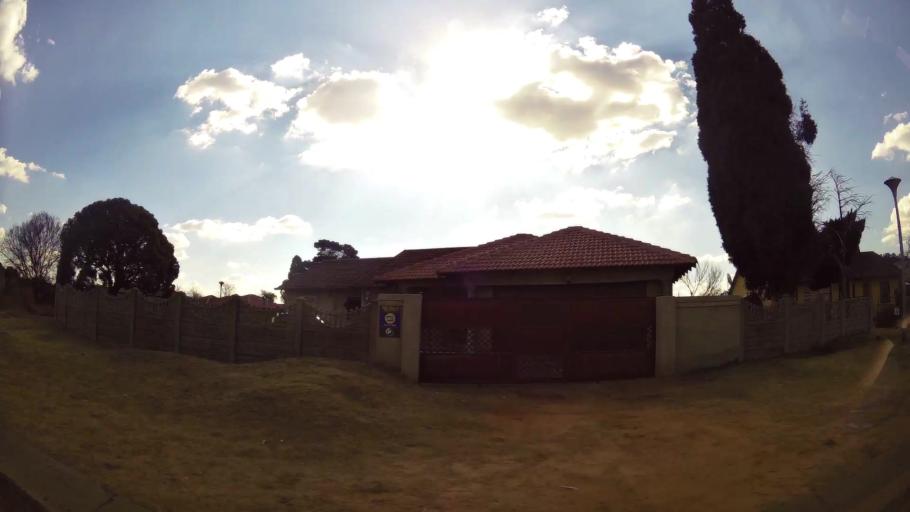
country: ZA
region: Mpumalanga
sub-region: Nkangala District Municipality
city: Witbank
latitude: -25.9289
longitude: 29.2175
